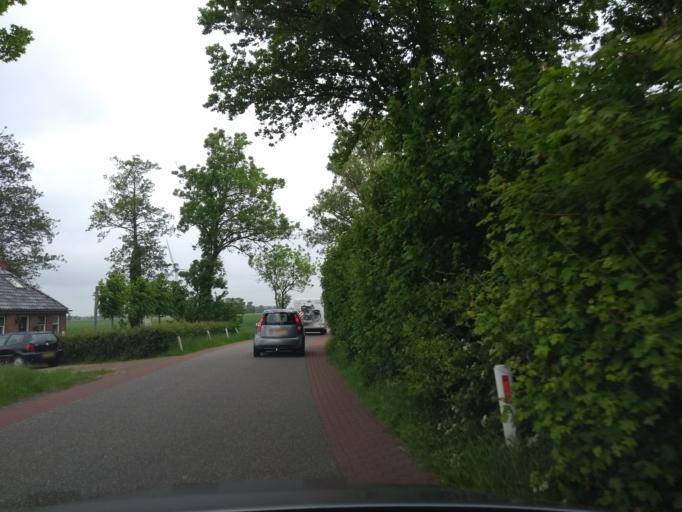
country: NL
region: Groningen
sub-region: Gemeente Zuidhorn
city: Oldehove
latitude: 53.3299
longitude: 6.4272
